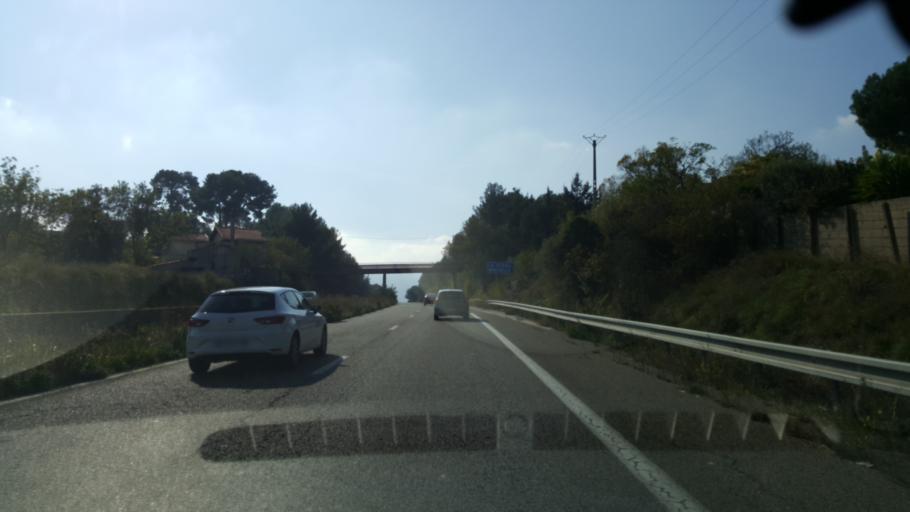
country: FR
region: Provence-Alpes-Cote d'Azur
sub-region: Departement des Bouches-du-Rhone
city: Aubagne
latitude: 43.3021
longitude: 5.5670
